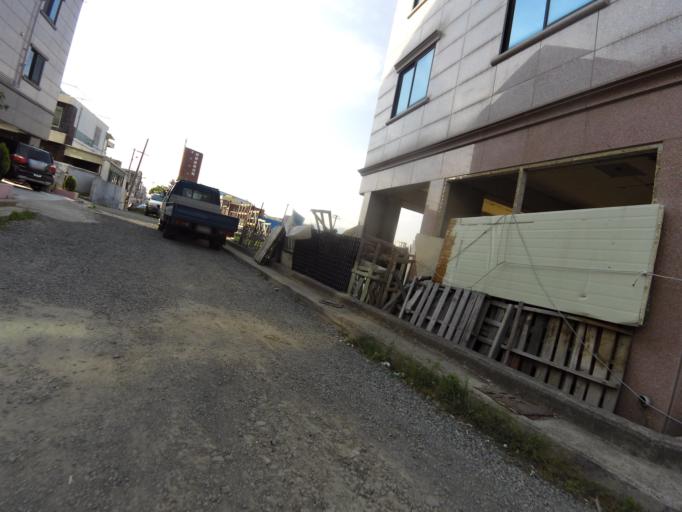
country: KR
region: Gyeongsangbuk-do
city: Gyeongsan-si
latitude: 35.8390
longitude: 128.7611
